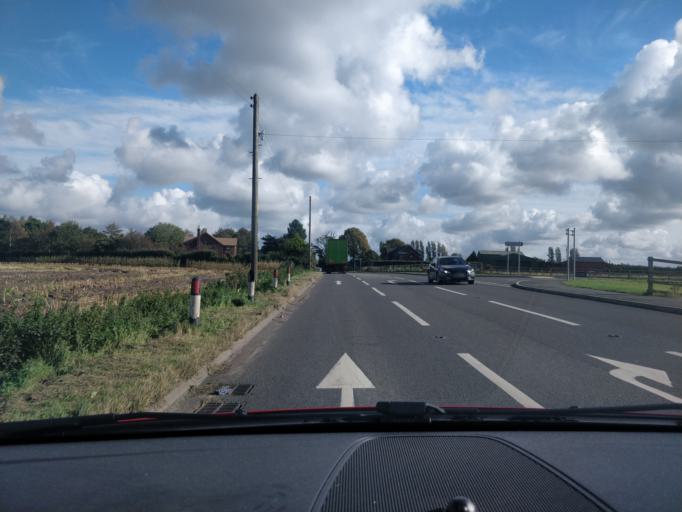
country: GB
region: England
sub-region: Lancashire
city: Ormskirk
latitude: 53.5904
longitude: -2.8838
